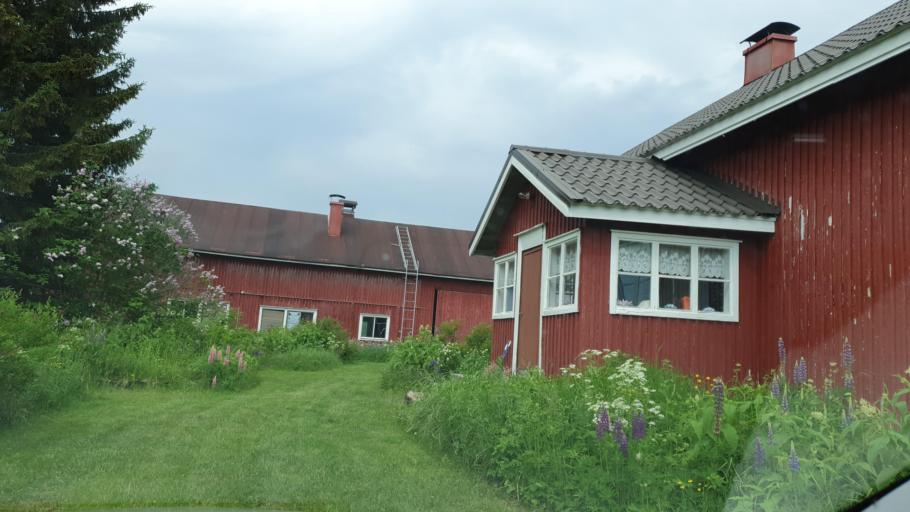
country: FI
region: Kainuu
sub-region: Kehys-Kainuu
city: Kuhmo
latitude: 64.3181
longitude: 29.8831
